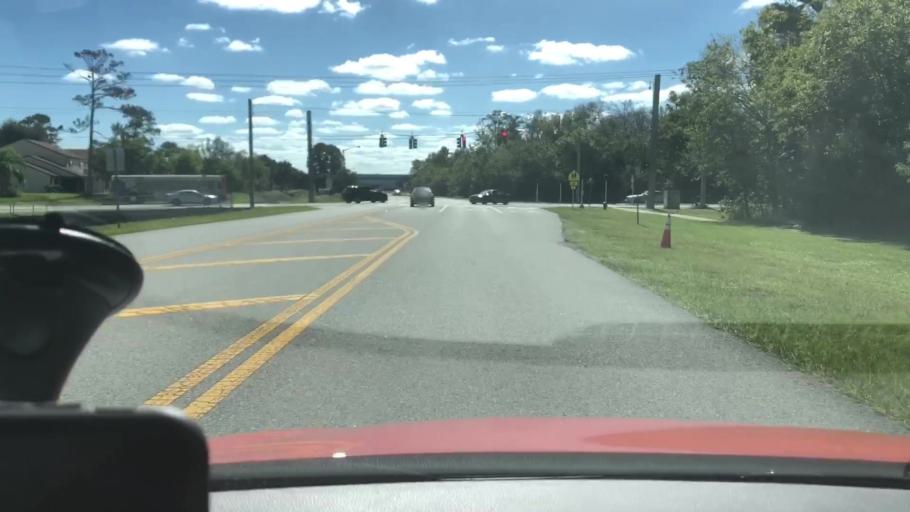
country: US
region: Florida
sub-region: Volusia County
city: Daytona Beach
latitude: 29.2037
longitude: -81.0662
